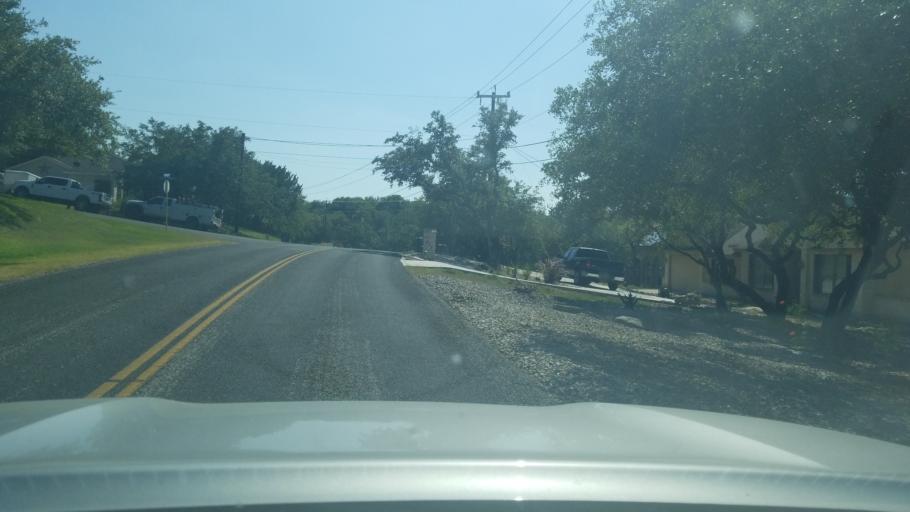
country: US
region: Texas
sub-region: Bexar County
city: Timberwood Park
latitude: 29.6821
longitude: -98.5009
